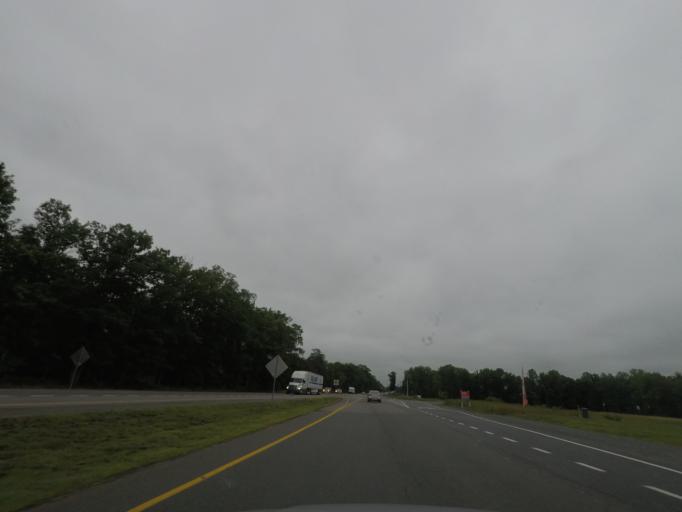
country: US
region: Virginia
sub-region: Fluvanna County
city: Palmyra
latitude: 37.9829
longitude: -78.2085
